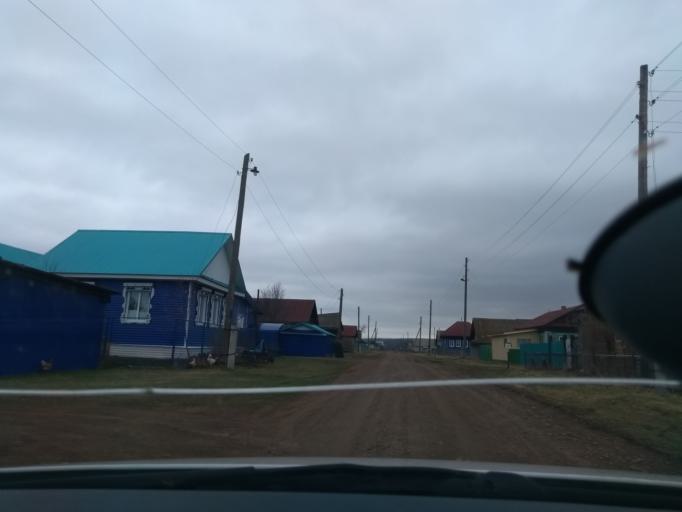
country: RU
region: Perm
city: Orda
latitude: 57.2203
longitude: 56.5932
